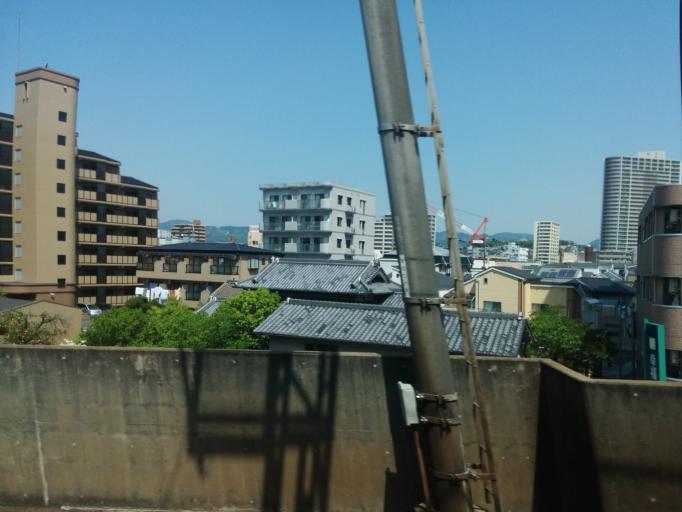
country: JP
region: Osaka
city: Takatsuki
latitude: 34.8468
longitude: 135.6166
